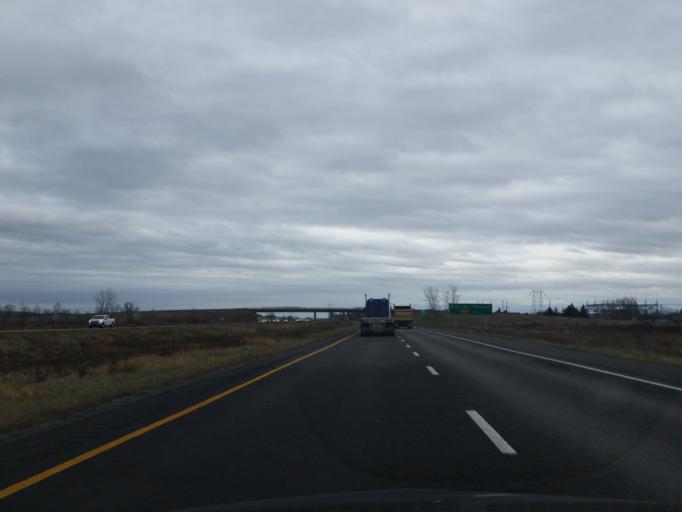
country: CA
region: Quebec
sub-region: Outaouais
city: Gatineau
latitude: 45.5110
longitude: -75.5942
